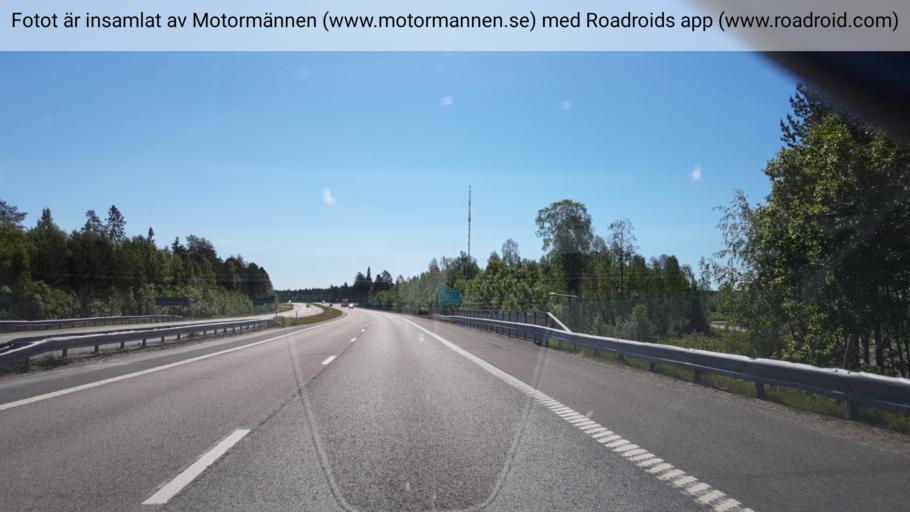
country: SE
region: Norrbotten
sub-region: Lulea Kommun
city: Gammelstad
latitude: 65.6280
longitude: 22.0472
